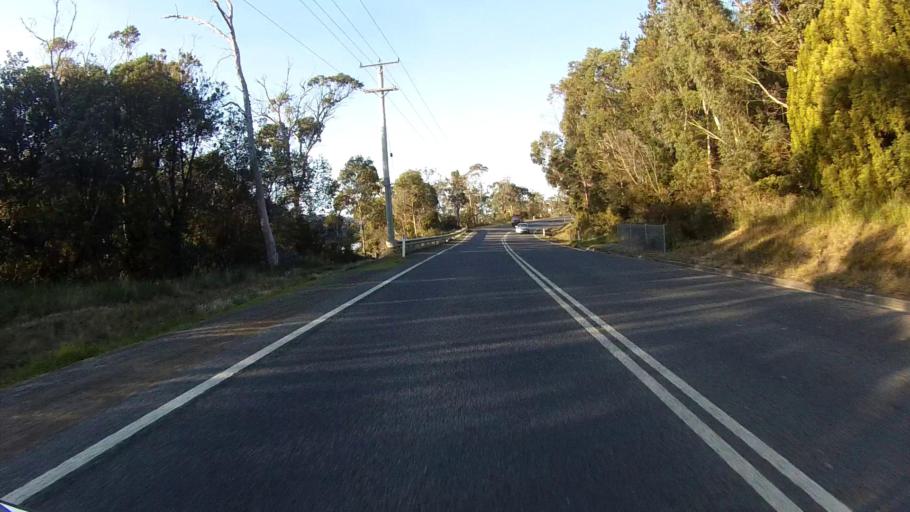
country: AU
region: Tasmania
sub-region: Clarence
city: Sandford
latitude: -43.0192
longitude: 147.9130
